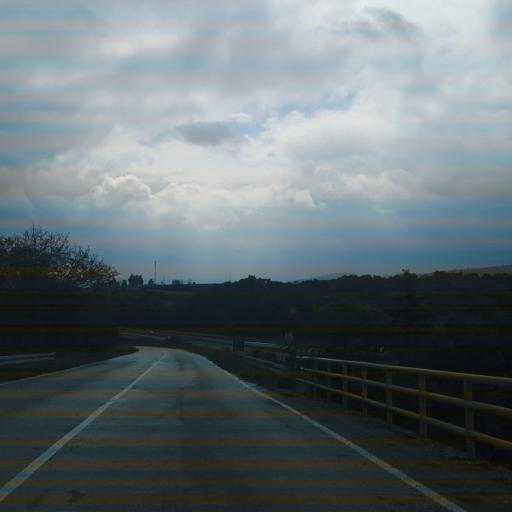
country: RS
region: Central Serbia
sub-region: Nisavski Okrug
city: Razanj
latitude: 43.6775
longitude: 21.5454
